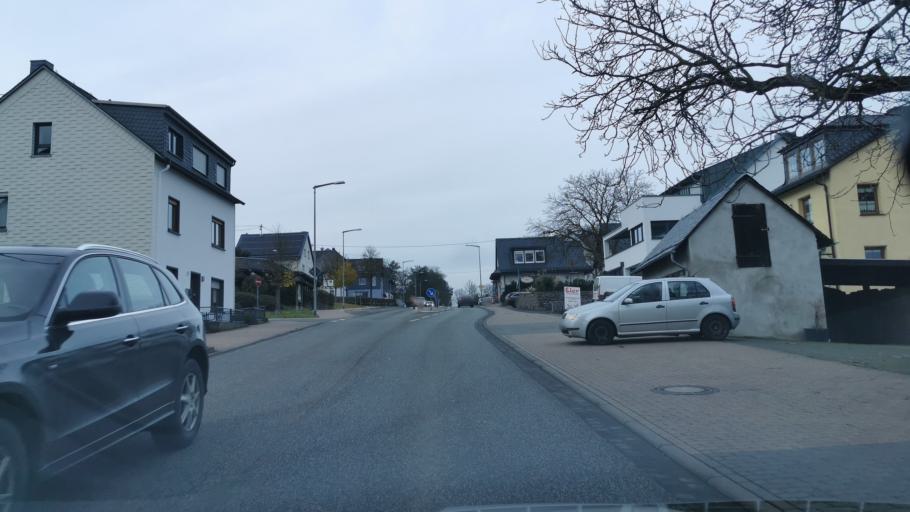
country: DE
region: Rheinland-Pfalz
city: Faid
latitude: 50.1457
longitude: 7.1212
